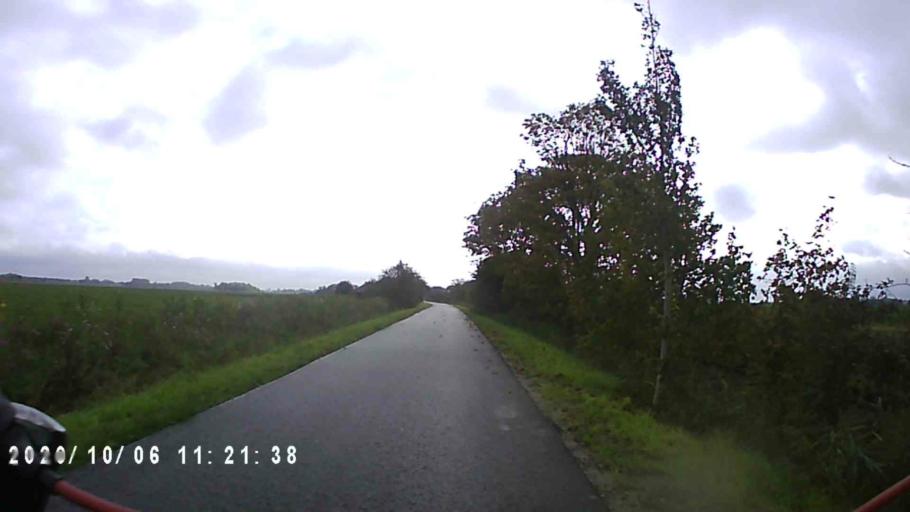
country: NL
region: Groningen
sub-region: Gemeente Zuidhorn
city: Oldehove
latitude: 53.3472
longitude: 6.4077
